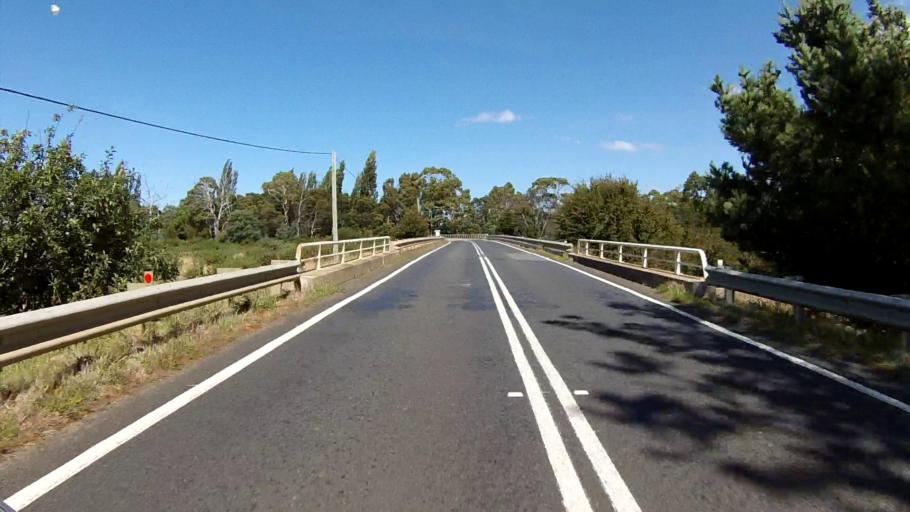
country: AU
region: Tasmania
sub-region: Break O'Day
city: St Helens
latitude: -42.0671
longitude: 148.0638
